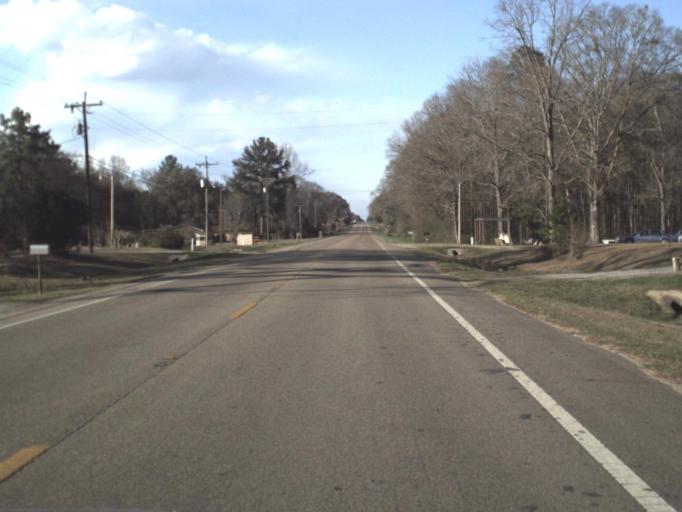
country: US
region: Florida
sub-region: Jackson County
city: Marianna
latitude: 30.7146
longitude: -85.2306
